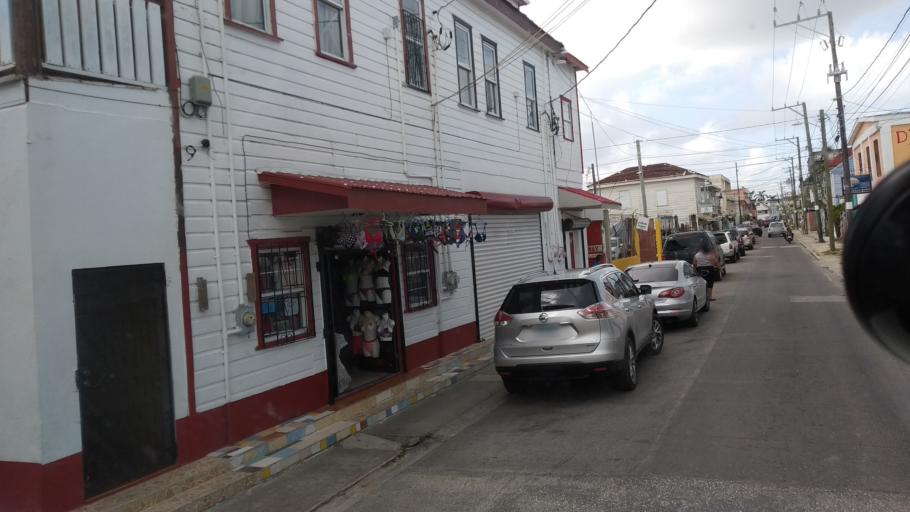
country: BZ
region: Belize
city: Belize City
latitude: 17.4979
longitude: -88.1866
